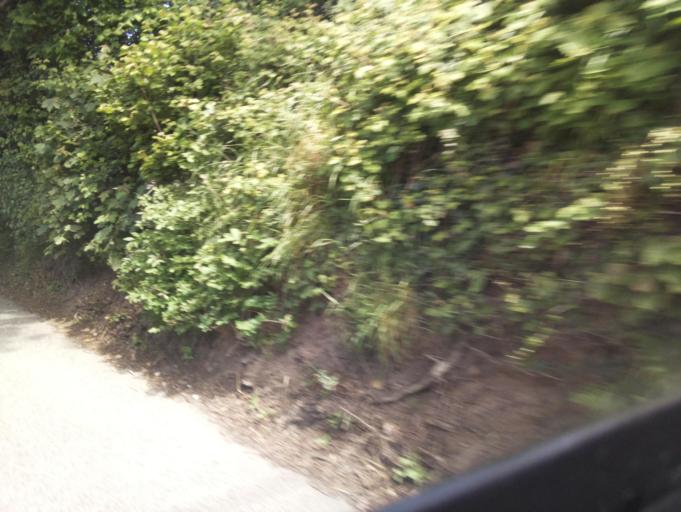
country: GB
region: England
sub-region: Devon
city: Uffculme
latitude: 50.8390
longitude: -3.3042
